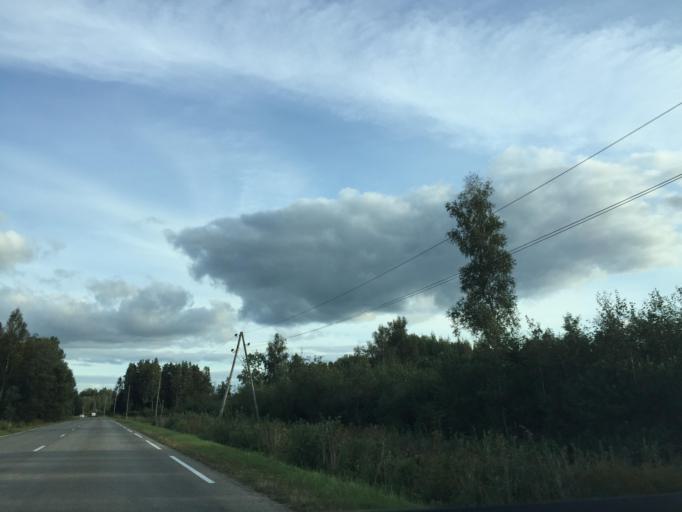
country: LV
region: Nereta
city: Nereta
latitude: 56.2998
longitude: 25.1088
